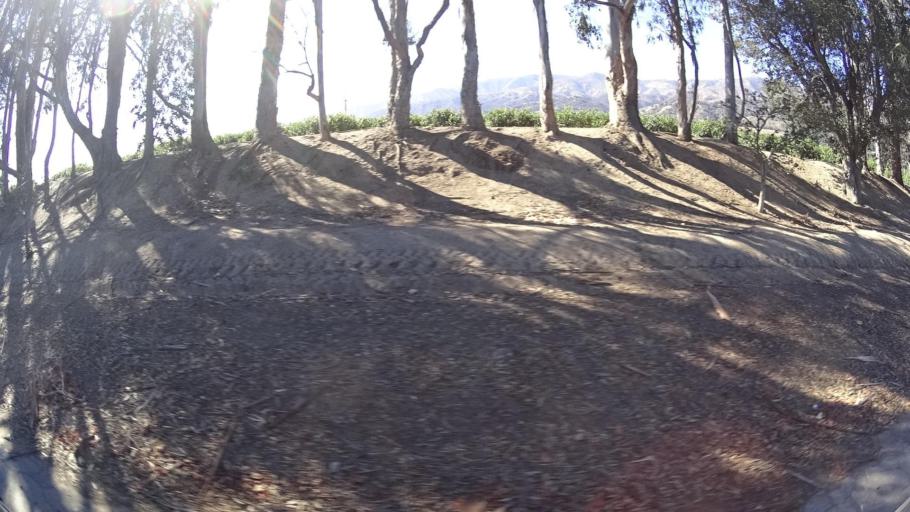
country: US
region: California
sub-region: Monterey County
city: Gonzales
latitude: 36.4722
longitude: -121.4769
